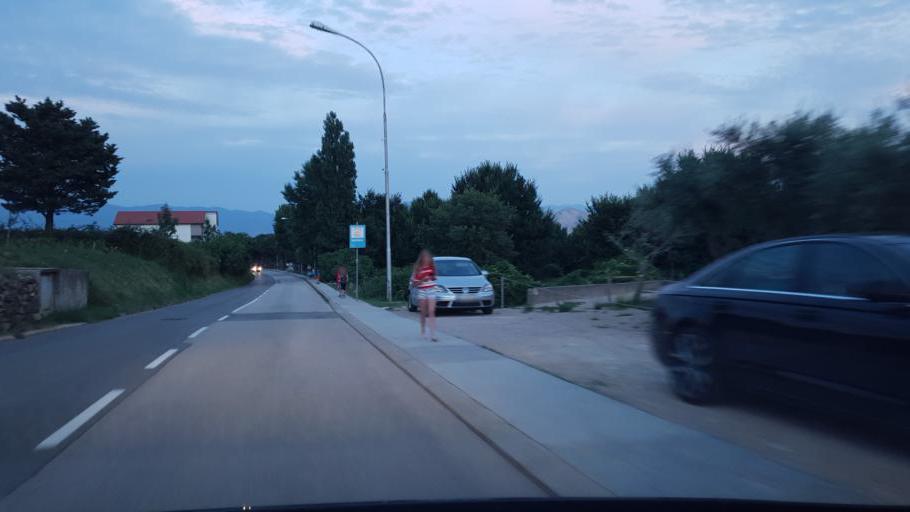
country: HR
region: Primorsko-Goranska
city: Punat
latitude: 44.9730
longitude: 14.7418
